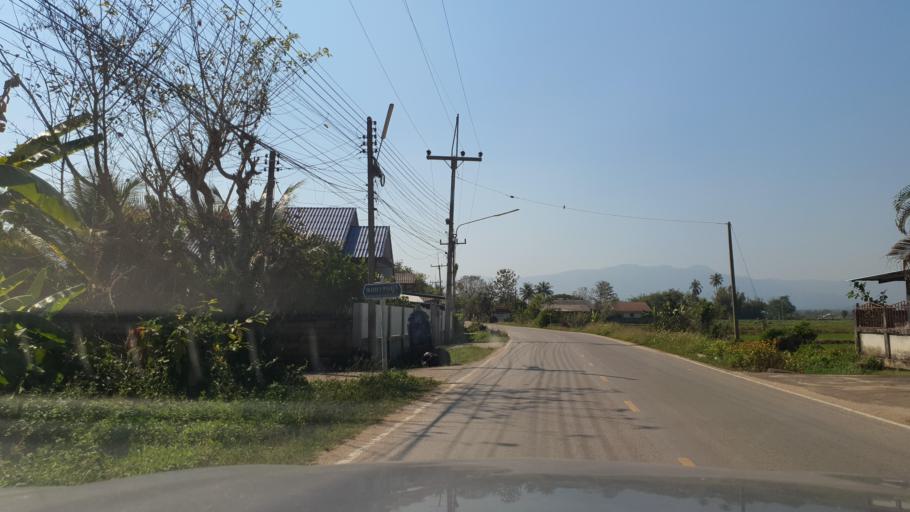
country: TH
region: Chiang Rai
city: Mae Lao
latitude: 19.7634
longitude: 99.7233
